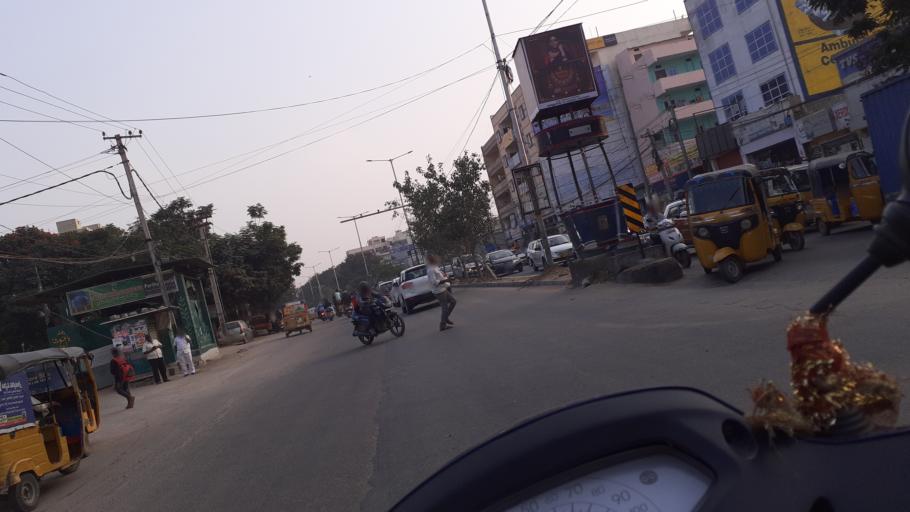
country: IN
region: Telangana
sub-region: Rangareddi
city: Kukatpalli
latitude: 17.4761
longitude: 78.3631
